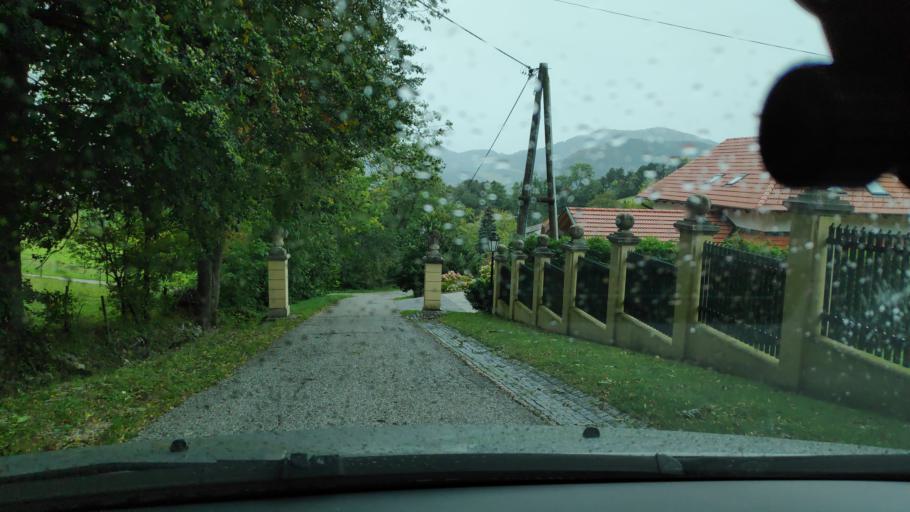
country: AT
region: Lower Austria
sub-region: Politischer Bezirk Neunkirchen
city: Grunbach am Schneeberg
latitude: 47.8068
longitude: 15.9915
